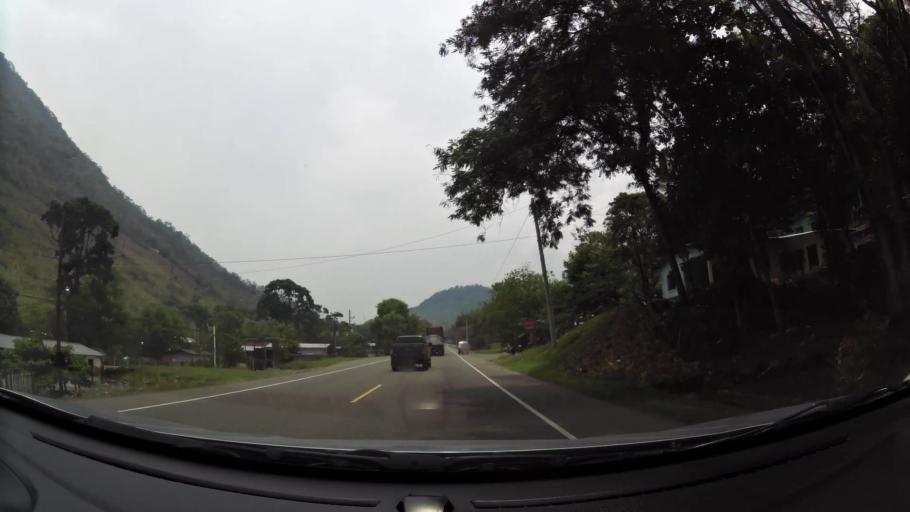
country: HN
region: Comayagua
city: Taulabe
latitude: 14.7440
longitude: -87.9618
